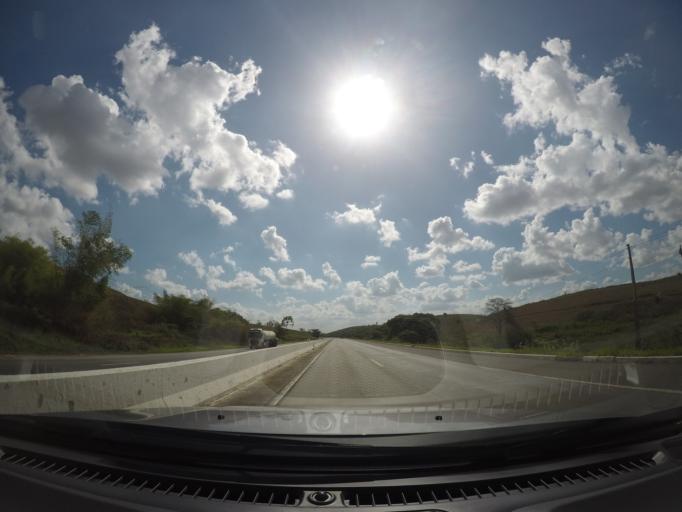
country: BR
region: Pernambuco
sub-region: Ribeirao
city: Ribeirao
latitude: -8.4376
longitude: -35.3314
